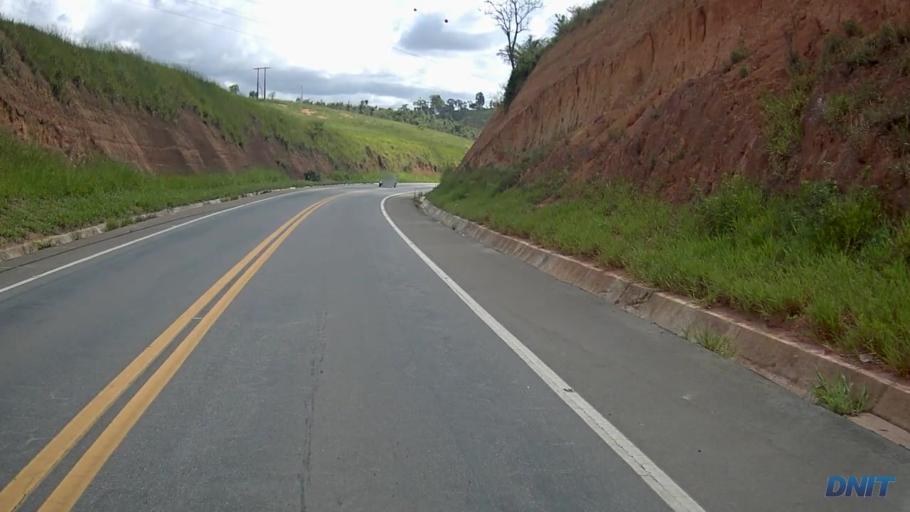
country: BR
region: Minas Gerais
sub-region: Belo Oriente
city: Belo Oriente
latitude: -19.0901
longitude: -42.1888
